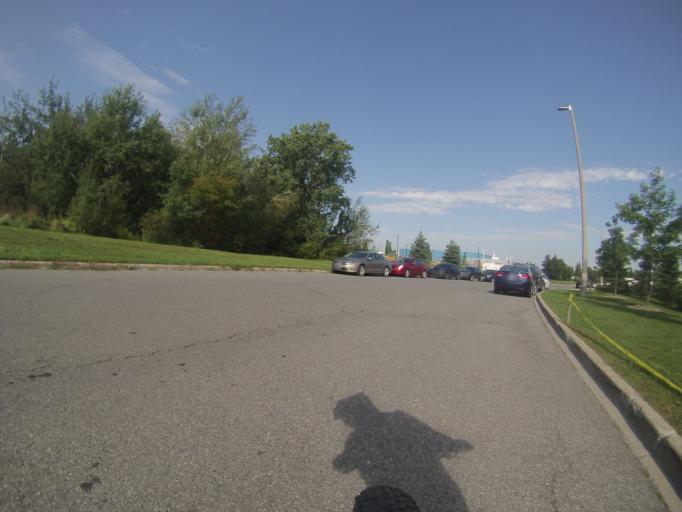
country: CA
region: Ontario
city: Ottawa
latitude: 45.3774
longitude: -75.6147
